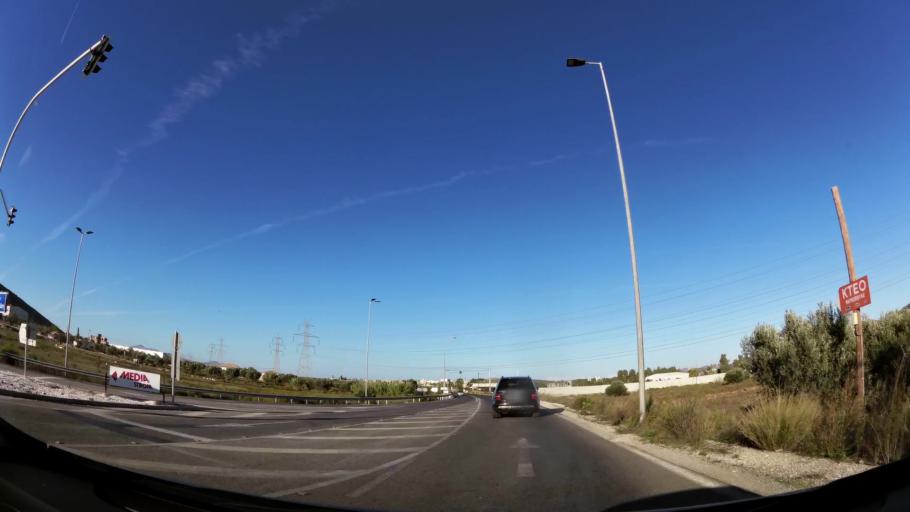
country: GR
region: Attica
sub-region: Nomarchia Anatolikis Attikis
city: Markopoulo
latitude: 37.8632
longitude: 23.9246
